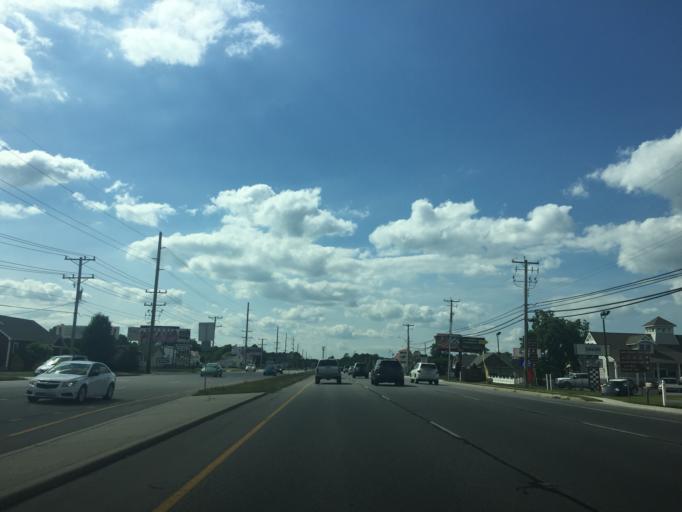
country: US
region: Delaware
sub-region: Sussex County
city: Lewes
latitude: 38.7414
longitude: -75.1482
